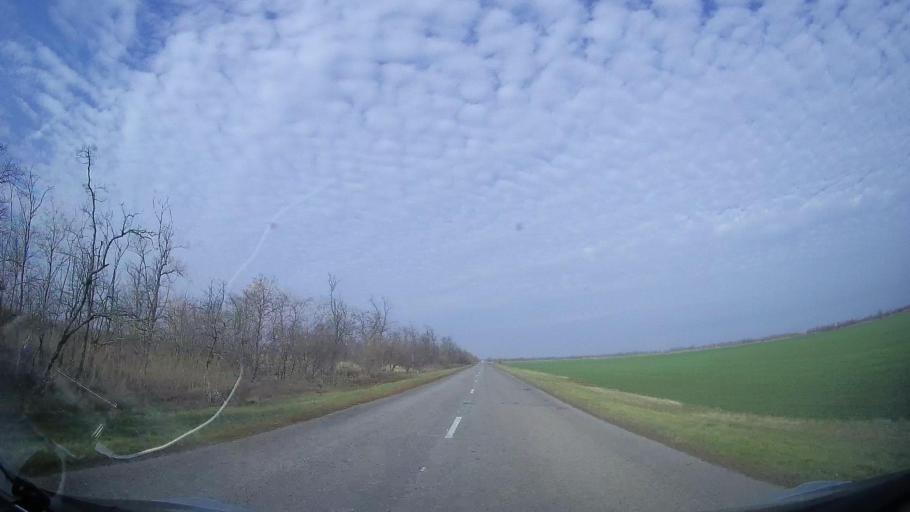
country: RU
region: Rostov
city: Gigant
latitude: 46.8670
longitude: 41.2766
